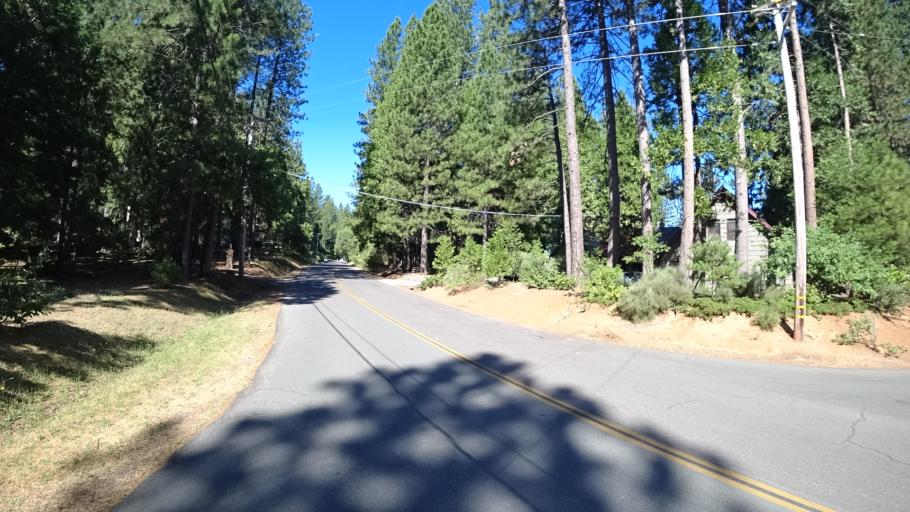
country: US
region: California
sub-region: Calaveras County
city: Arnold
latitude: 38.2527
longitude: -120.3671
